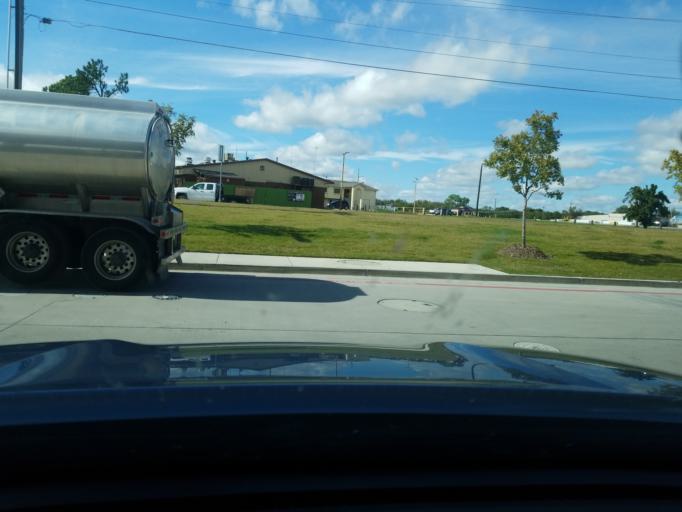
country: US
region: Texas
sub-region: Parker County
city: Weatherford
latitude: 32.7297
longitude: -97.8203
